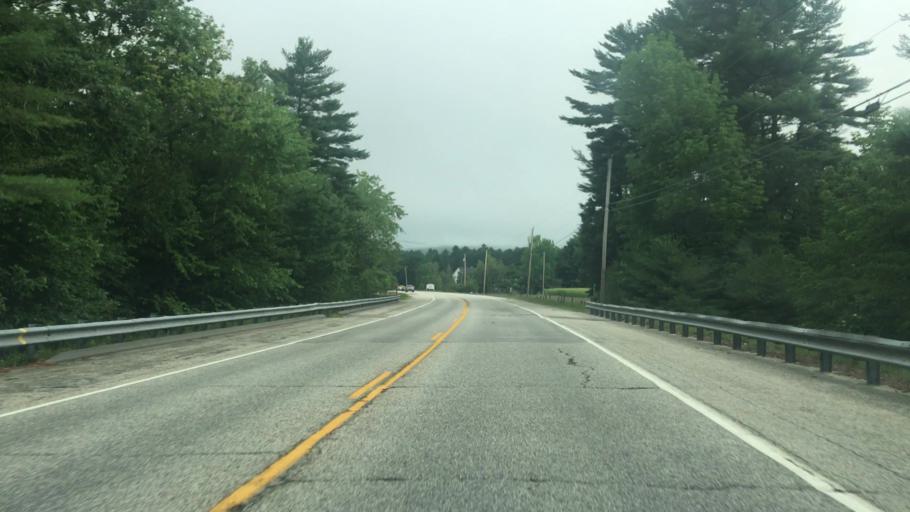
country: US
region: Maine
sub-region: Oxford County
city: Paris
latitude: 44.2755
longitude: -70.5142
